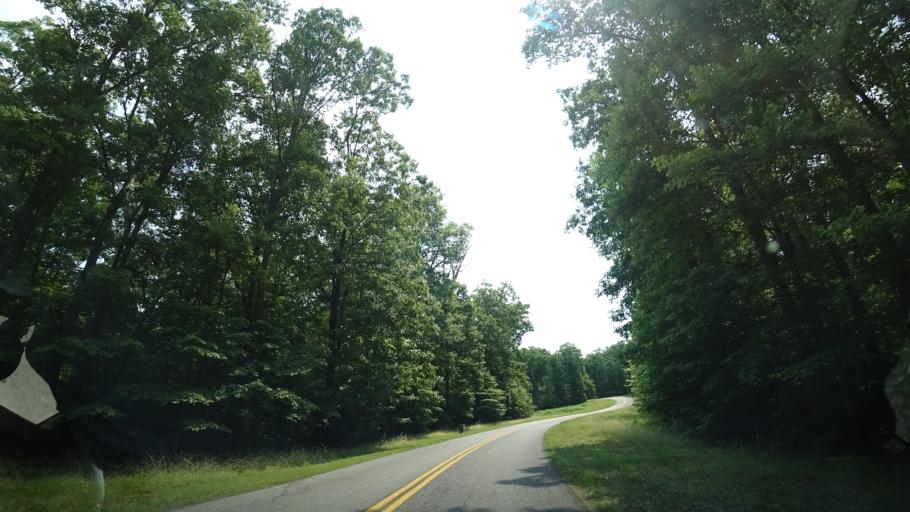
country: US
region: Virginia
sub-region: Louisa County
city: Louisa
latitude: 38.1142
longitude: -77.8167
